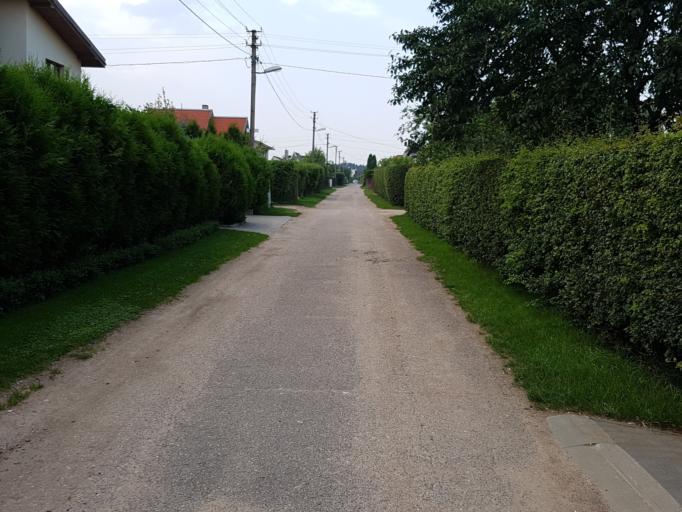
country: LT
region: Vilnius County
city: Rasos
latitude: 54.7897
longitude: 25.3587
